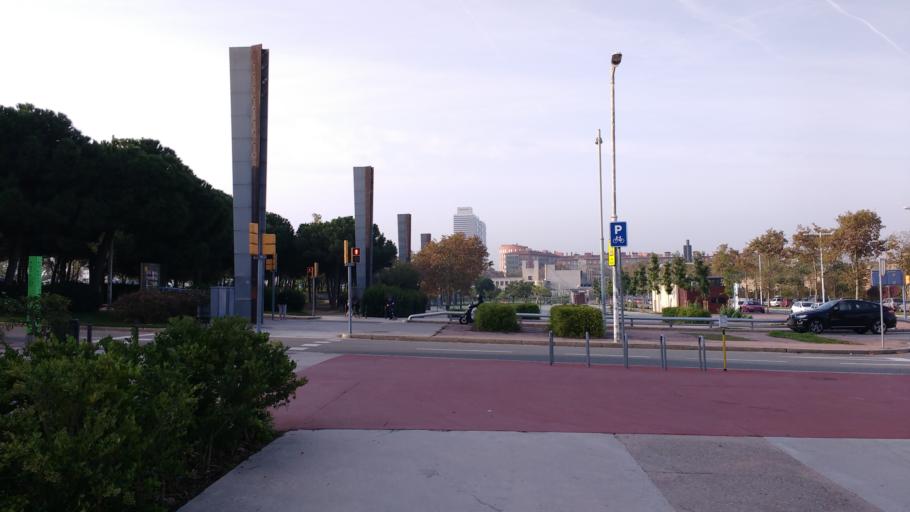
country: ES
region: Catalonia
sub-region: Provincia de Barcelona
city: Sant Marti
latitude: 41.3964
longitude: 2.2056
